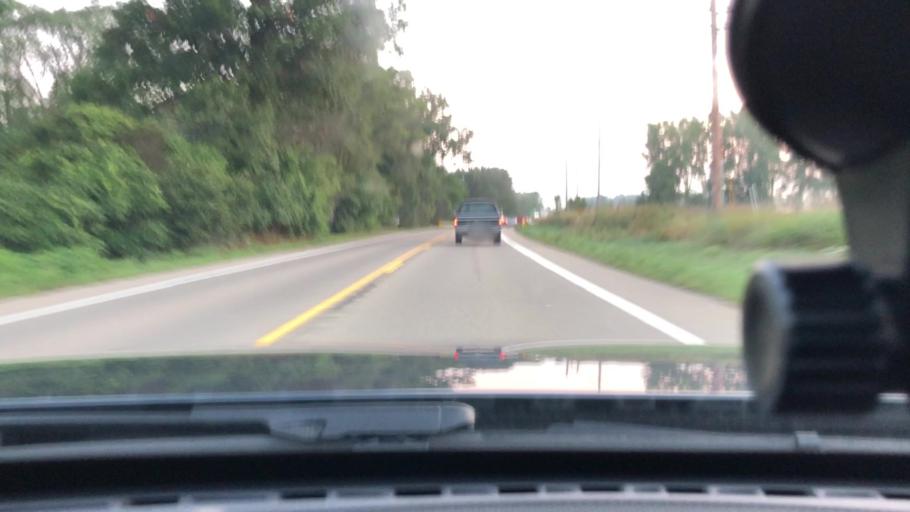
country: US
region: Michigan
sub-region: Washtenaw County
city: Chelsea
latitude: 42.2506
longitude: -84.0337
